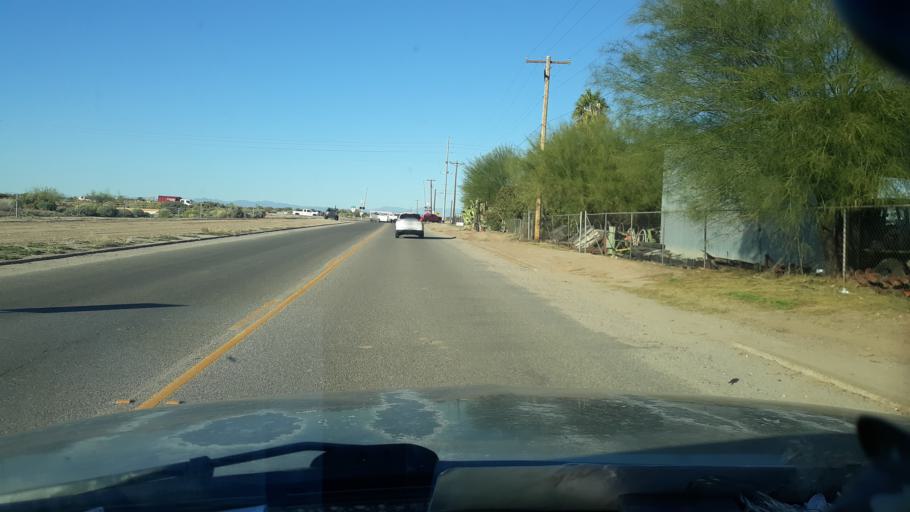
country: US
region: Arizona
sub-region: Maricopa County
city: Citrus Park
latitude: 33.5646
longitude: -112.3936
